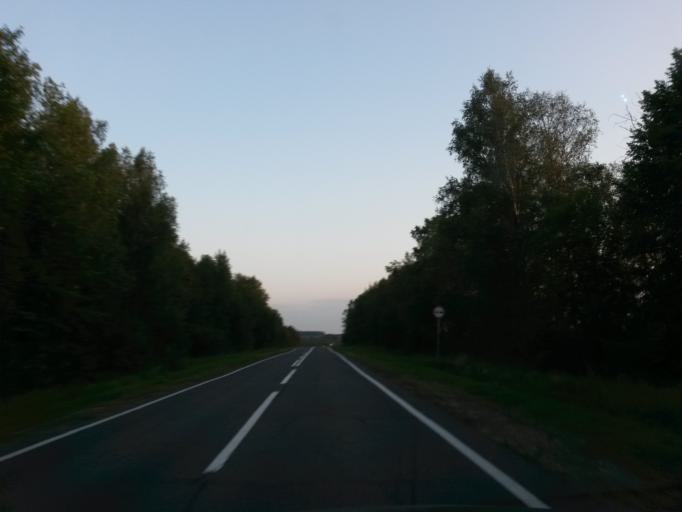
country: RU
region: Jaroslavl
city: Tutayev
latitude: 57.9462
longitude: 39.4970
